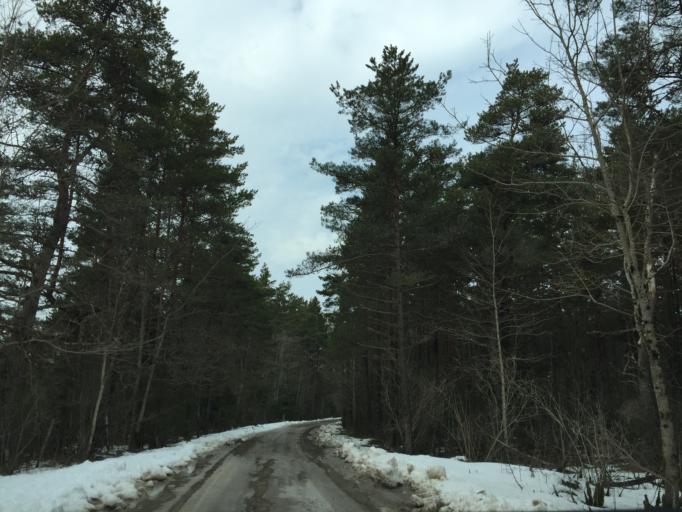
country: EE
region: Saare
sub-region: Kuressaare linn
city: Kuressaare
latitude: 58.4309
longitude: 22.1439
